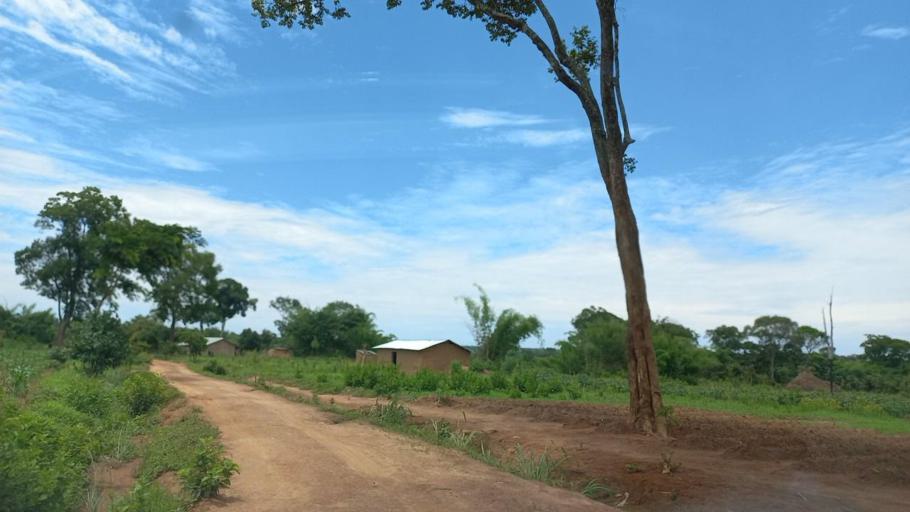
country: ZM
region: Copperbelt
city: Kitwe
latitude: -12.8140
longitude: 28.3923
